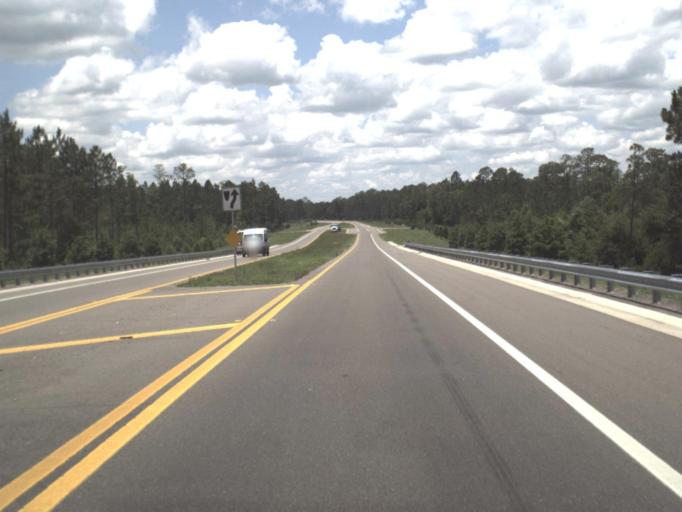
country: US
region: Florida
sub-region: Alachua County
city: Waldo
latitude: 29.7146
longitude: -82.1425
